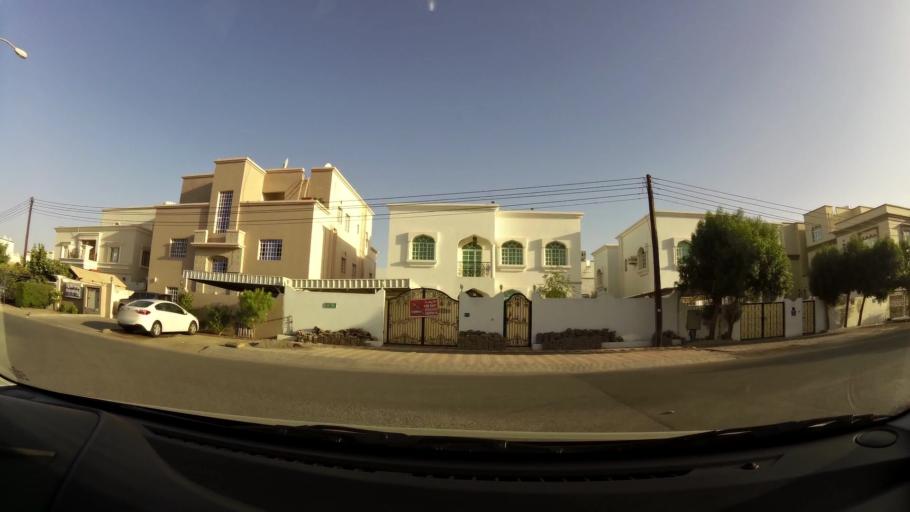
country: OM
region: Muhafazat Masqat
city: As Sib al Jadidah
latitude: 23.6117
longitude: 58.2317
